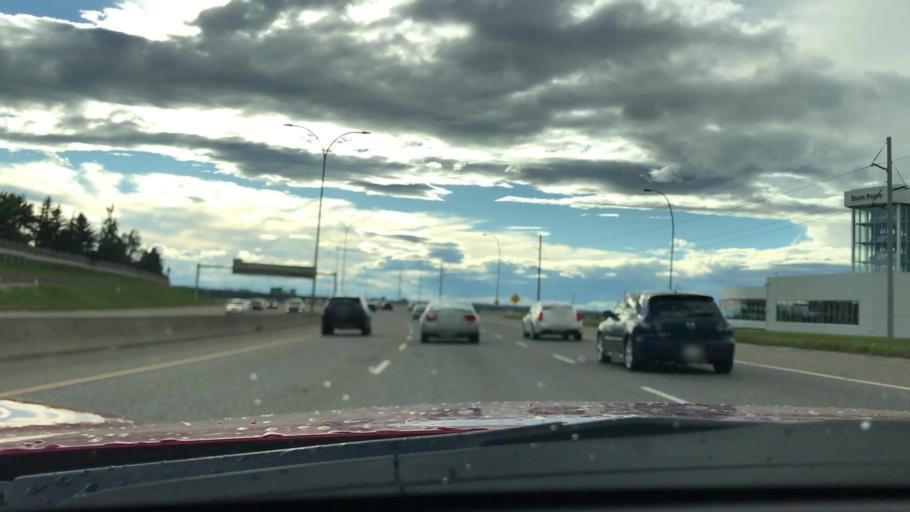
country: CA
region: Alberta
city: Calgary
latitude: 50.9456
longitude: -113.9833
